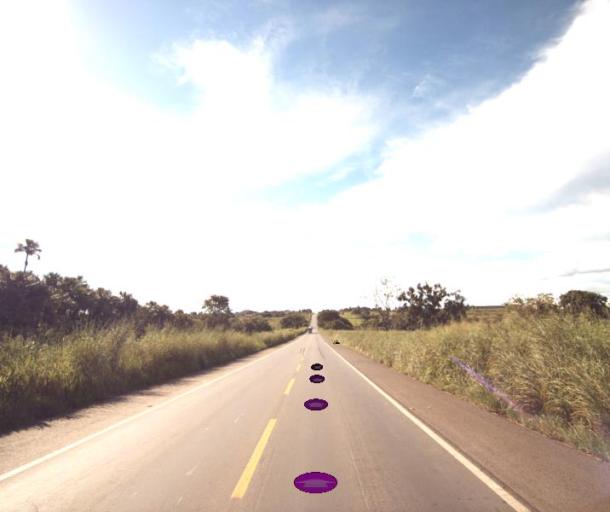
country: BR
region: Goias
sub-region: Rialma
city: Rialma
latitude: -15.4601
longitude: -49.5013
